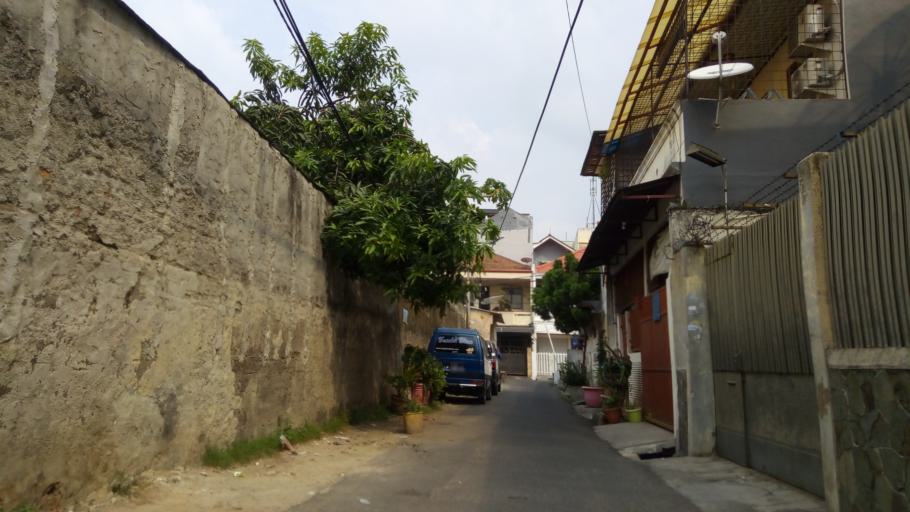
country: ID
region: Jakarta Raya
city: Jakarta
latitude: -6.1561
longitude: 106.8354
